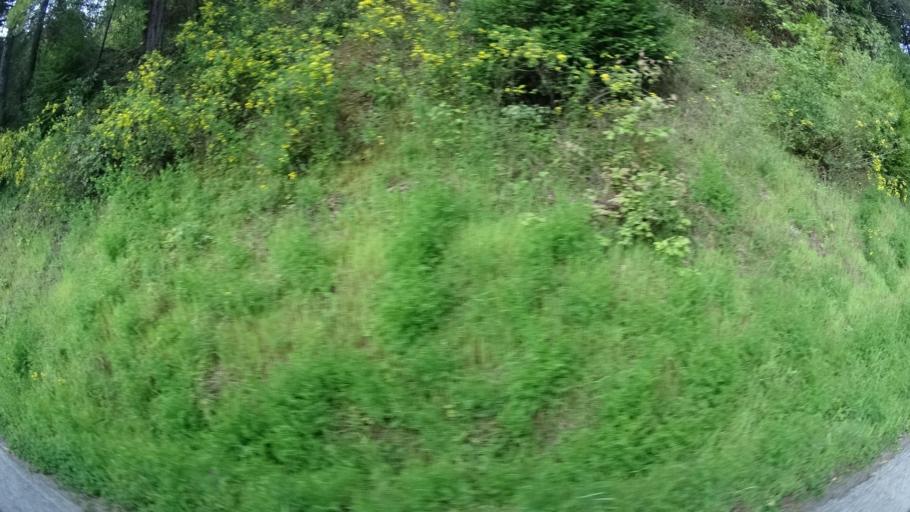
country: US
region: California
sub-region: Humboldt County
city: Redway
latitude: 40.2231
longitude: -123.8253
